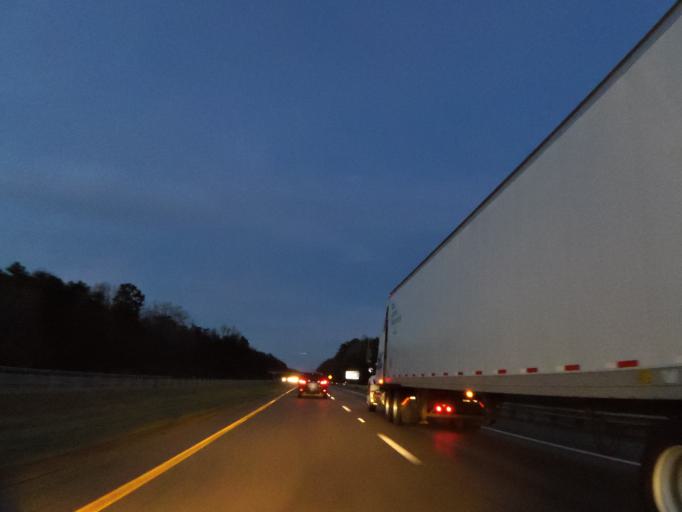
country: US
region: Kentucky
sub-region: Whitley County
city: Corbin
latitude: 36.8916
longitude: -84.1462
